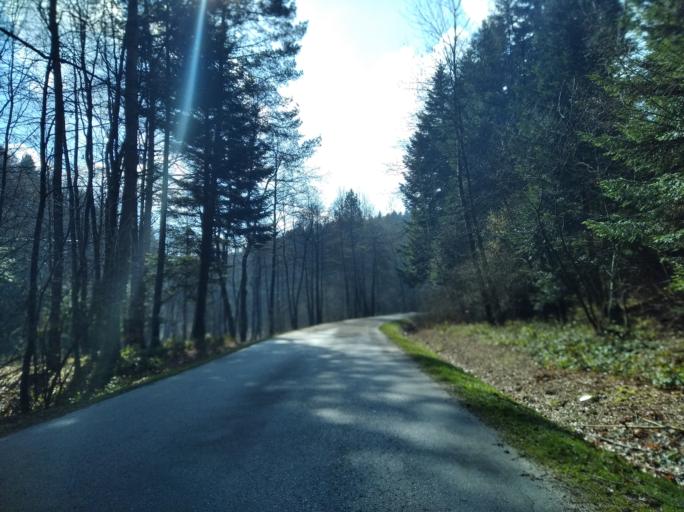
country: PL
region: Subcarpathian Voivodeship
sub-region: Powiat strzyzowski
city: Frysztak
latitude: 49.8648
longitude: 21.5504
